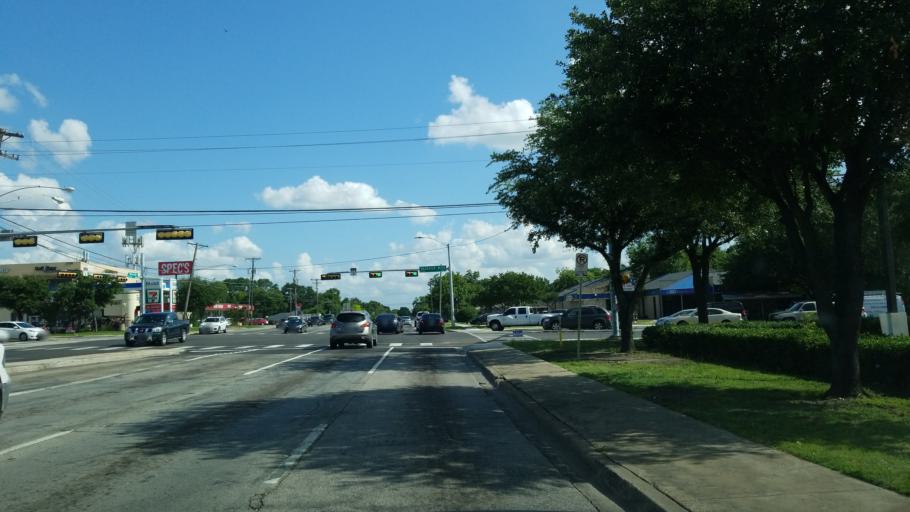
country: US
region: Texas
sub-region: Dallas County
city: Farmers Branch
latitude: 32.8810
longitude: -96.8563
